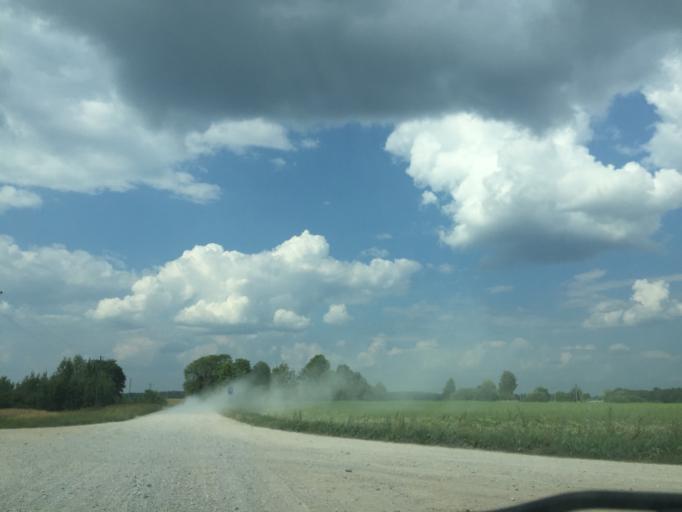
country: LV
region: Auces Novads
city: Auce
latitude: 56.4012
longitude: 23.0584
